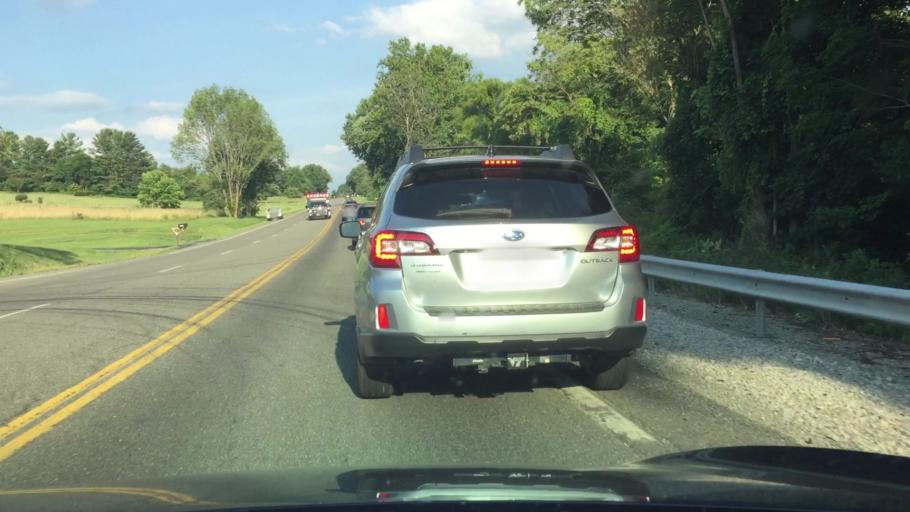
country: US
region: Virginia
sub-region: Montgomery County
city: Christiansburg
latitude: 37.1316
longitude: -80.4555
